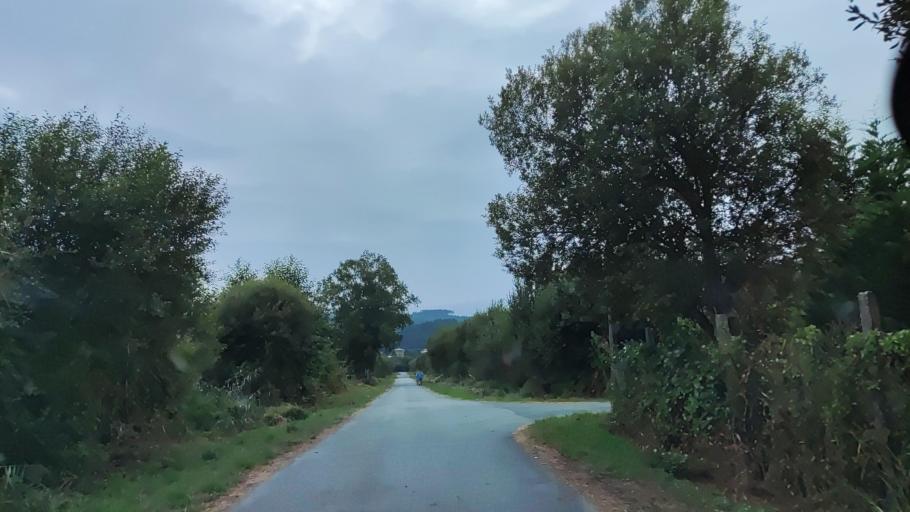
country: ES
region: Galicia
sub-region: Provincia da Coruna
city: Rois
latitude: 42.7150
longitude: -8.7098
